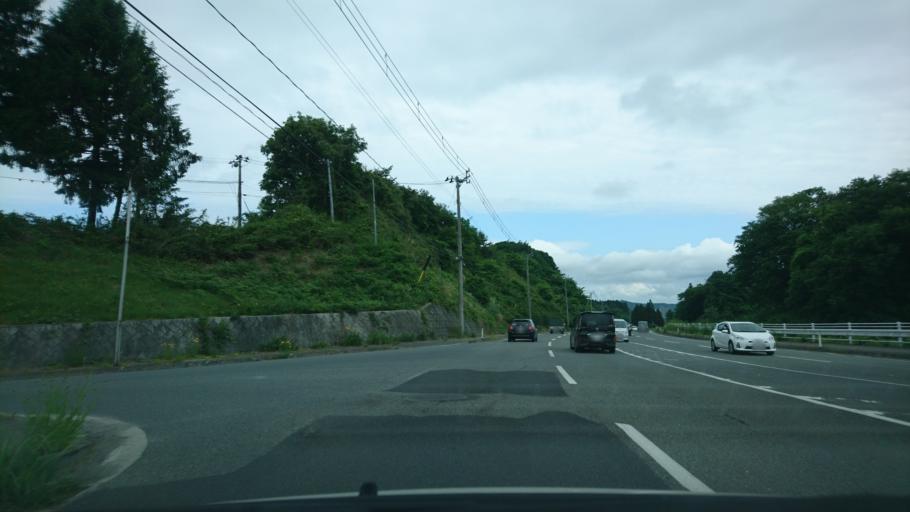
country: JP
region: Iwate
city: Ichinoseki
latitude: 38.9095
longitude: 141.1458
